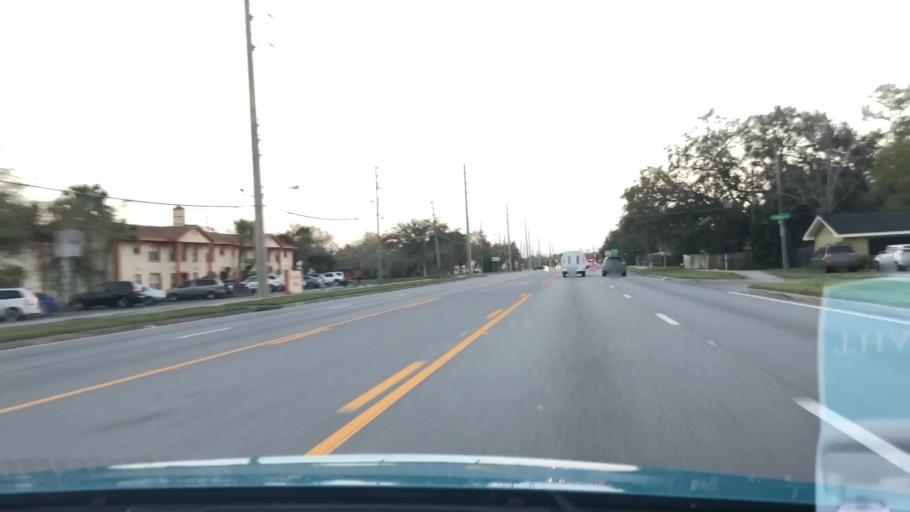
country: US
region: Florida
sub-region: Osceola County
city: Kissimmee
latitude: 28.3078
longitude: -81.3914
